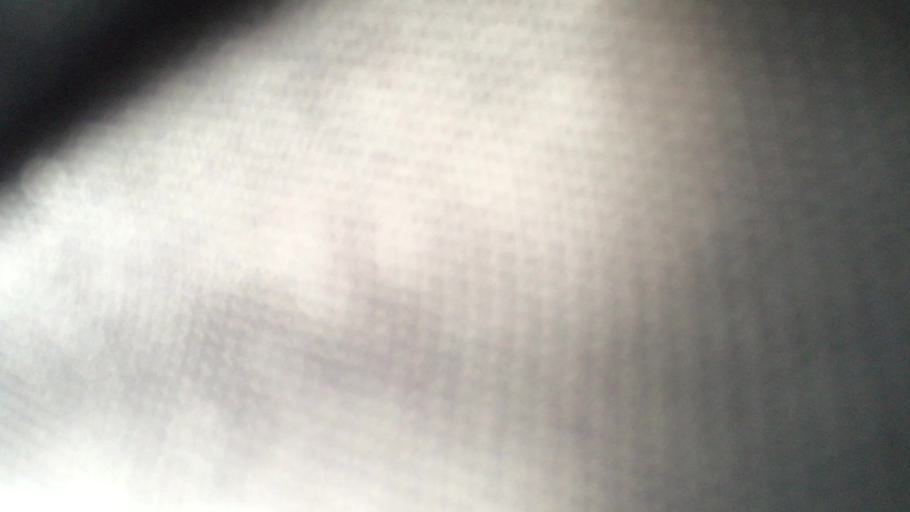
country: US
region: Maryland
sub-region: Somerset County
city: Princess Anne
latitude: 38.1601
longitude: -75.6904
